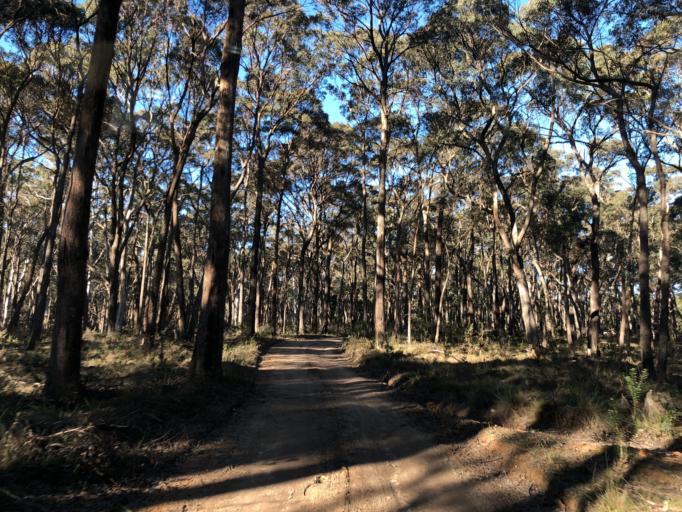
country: AU
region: Victoria
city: Brown Hill
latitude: -37.4972
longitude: 144.1731
